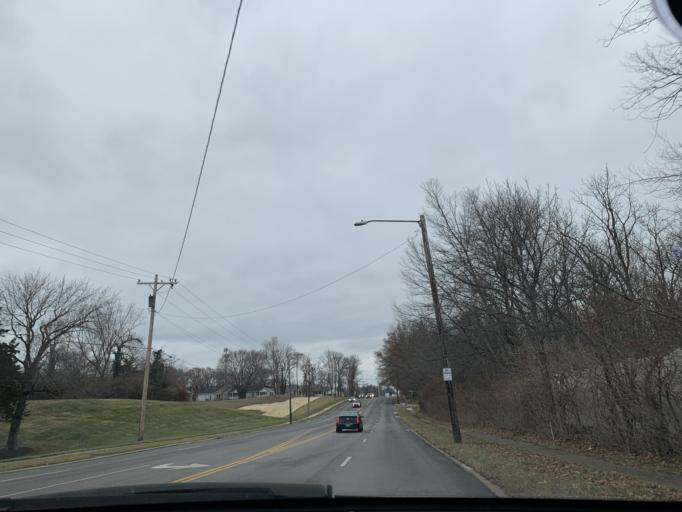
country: US
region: Illinois
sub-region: Sangamon County
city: Leland Grove
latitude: 39.7945
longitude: -89.6869
